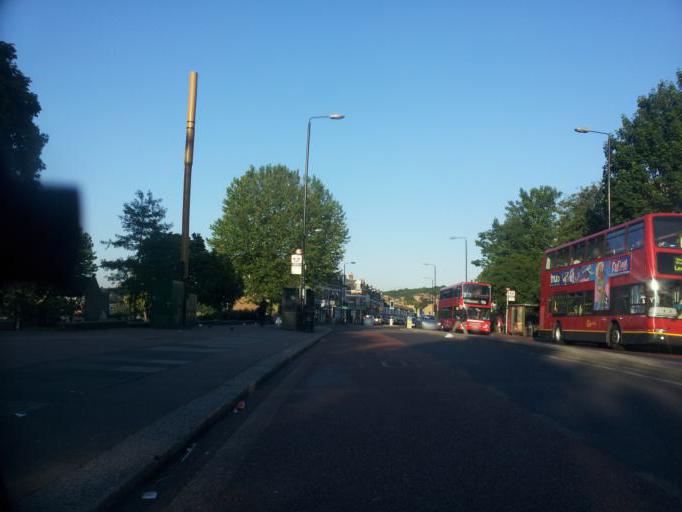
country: GB
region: England
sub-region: Greater London
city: Abbey Wood
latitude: 51.4858
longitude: 0.1004
